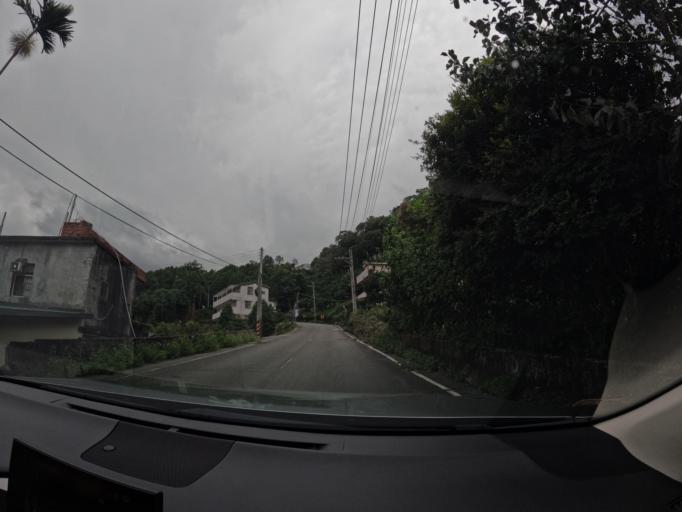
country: TW
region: Taiwan
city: Fengyuan
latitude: 24.3436
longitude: 120.8704
